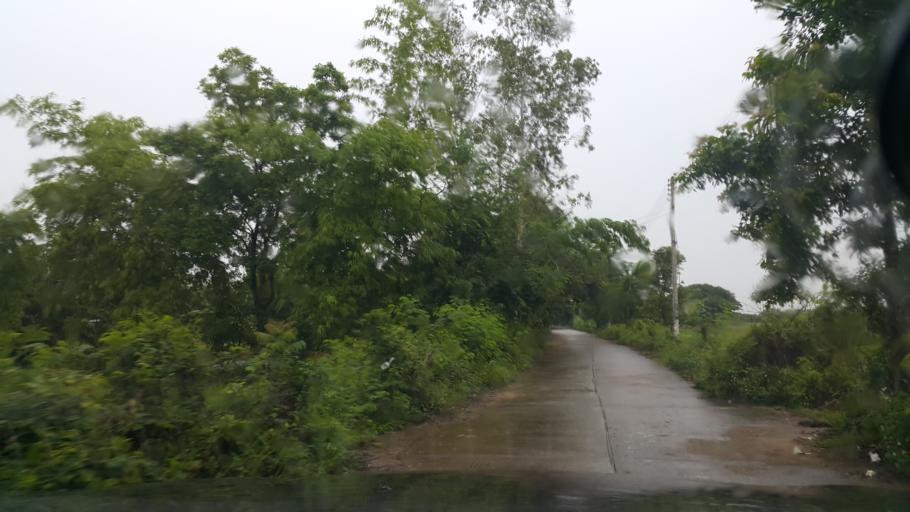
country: TH
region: Lamphun
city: Ban Thi
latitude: 18.6287
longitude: 99.1161
